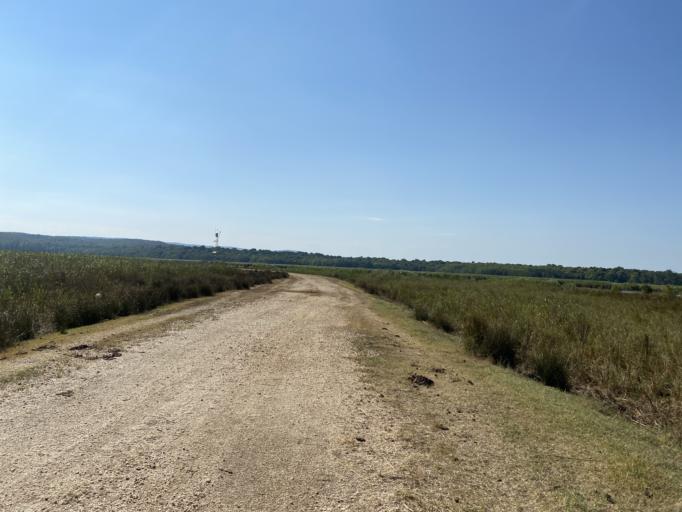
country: TR
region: Kirklareli
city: Igneada
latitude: 41.8615
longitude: 27.9718
